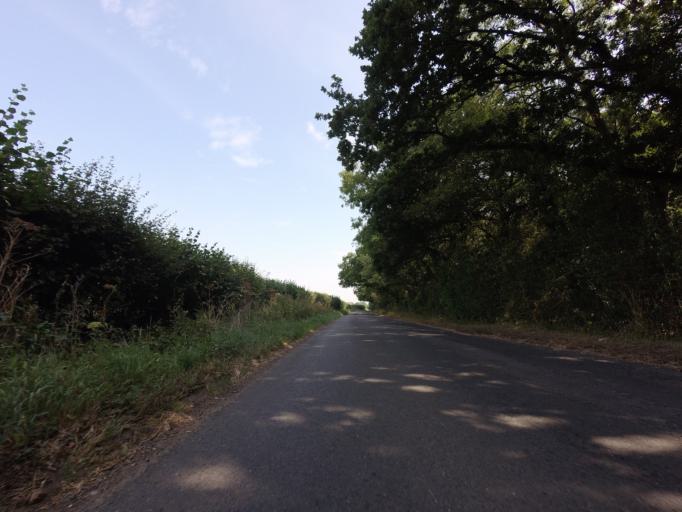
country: GB
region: England
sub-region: Kent
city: Headcorn
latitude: 51.1568
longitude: 0.6054
